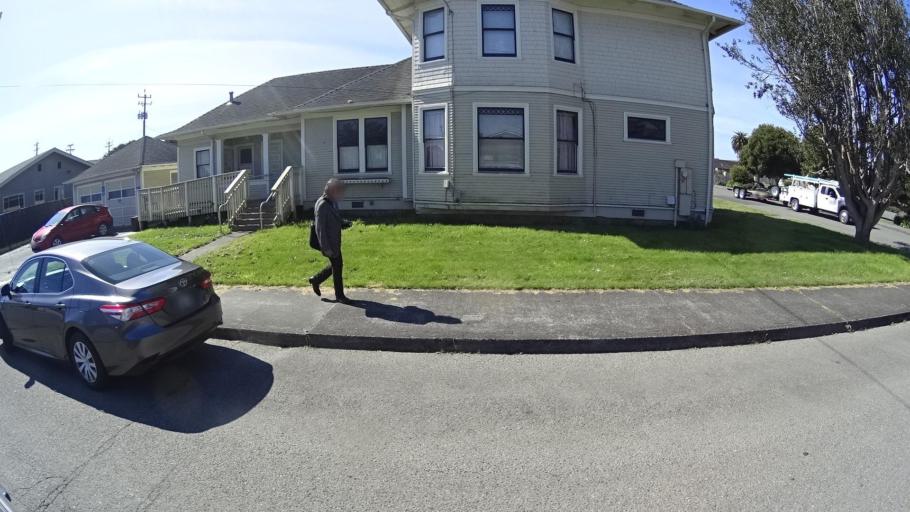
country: US
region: California
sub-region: Humboldt County
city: Eureka
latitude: 40.8055
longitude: -124.1567
